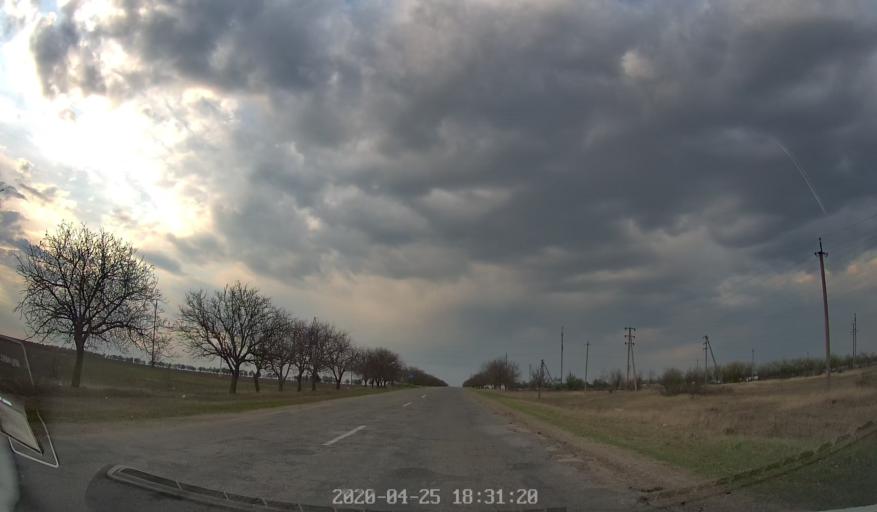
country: MD
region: Criuleni
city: Criuleni
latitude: 47.2162
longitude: 29.1476
